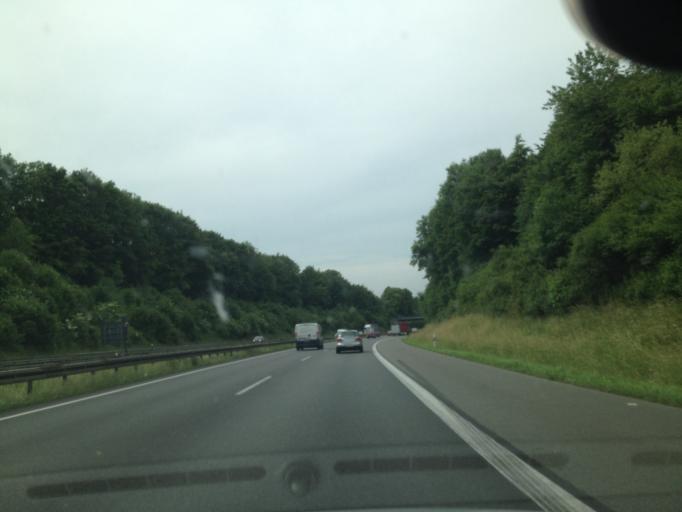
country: DE
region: North Rhine-Westphalia
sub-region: Regierungsbezirk Arnsberg
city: Schalksmuhle
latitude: 51.2903
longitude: 7.5594
